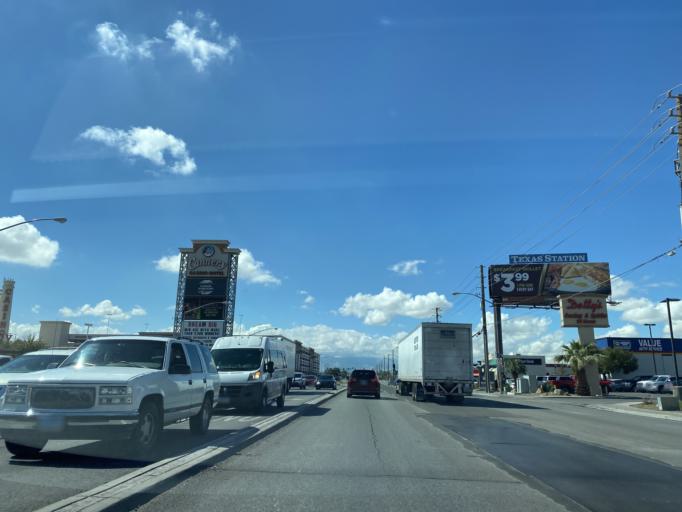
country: US
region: Nevada
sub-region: Clark County
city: North Las Vegas
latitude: 36.2398
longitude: -115.1169
